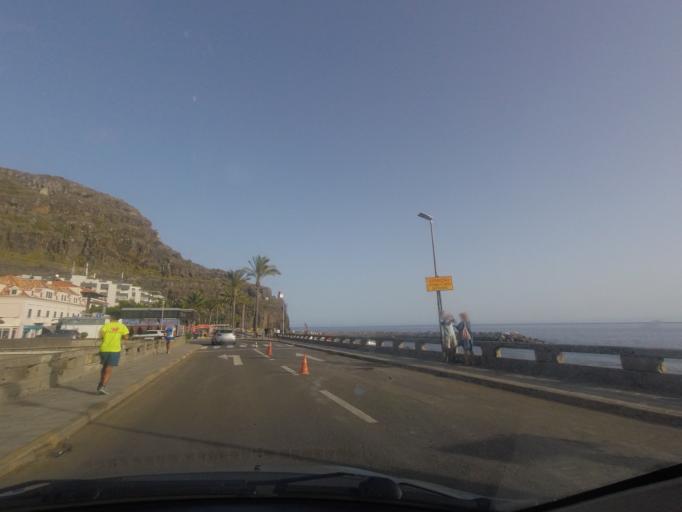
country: PT
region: Madeira
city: Ribeira Brava
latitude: 32.6709
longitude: -17.0660
